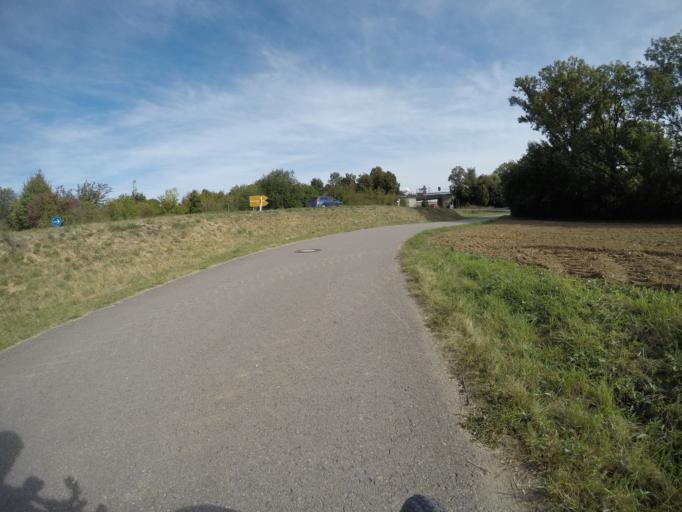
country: DE
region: Baden-Wuerttemberg
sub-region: Regierungsbezirk Stuttgart
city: Schwieberdingen
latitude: 48.8645
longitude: 9.0966
